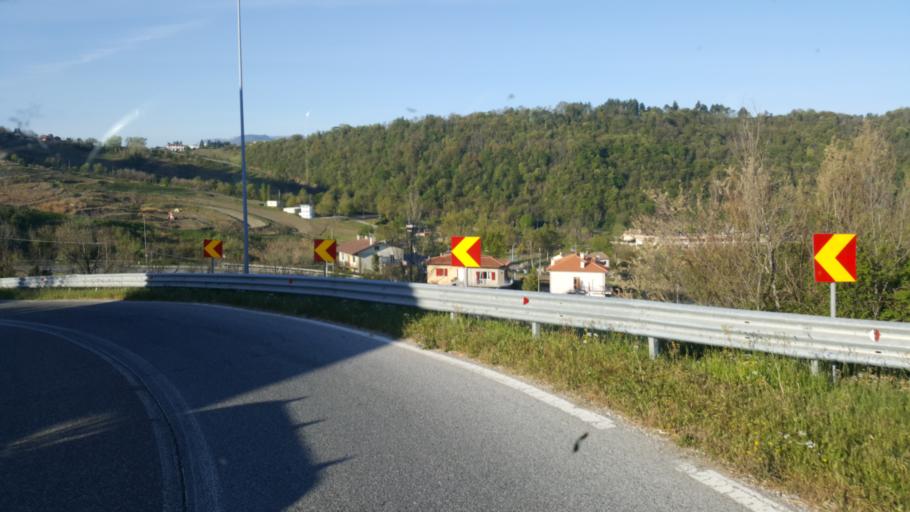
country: SM
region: Borgo Maggiore
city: Borgo Maggiore
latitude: 43.9461
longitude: 12.4381
